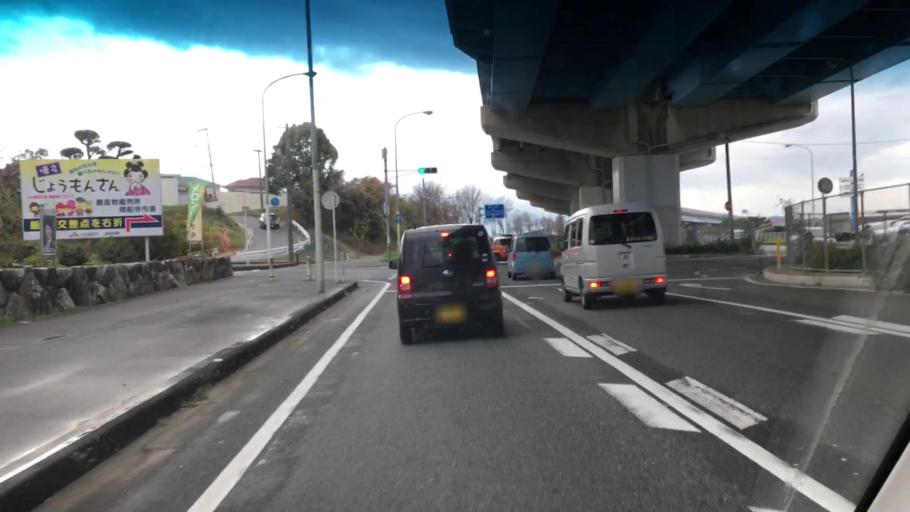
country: JP
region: Fukuoka
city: Maebaru-chuo
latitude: 33.5682
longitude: 130.2475
